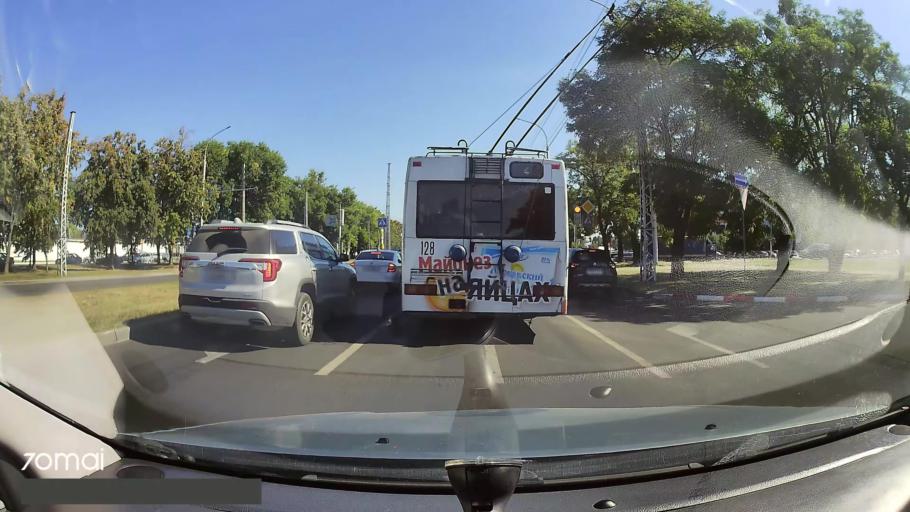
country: BY
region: Brest
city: Brest
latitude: 52.1134
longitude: 23.7705
